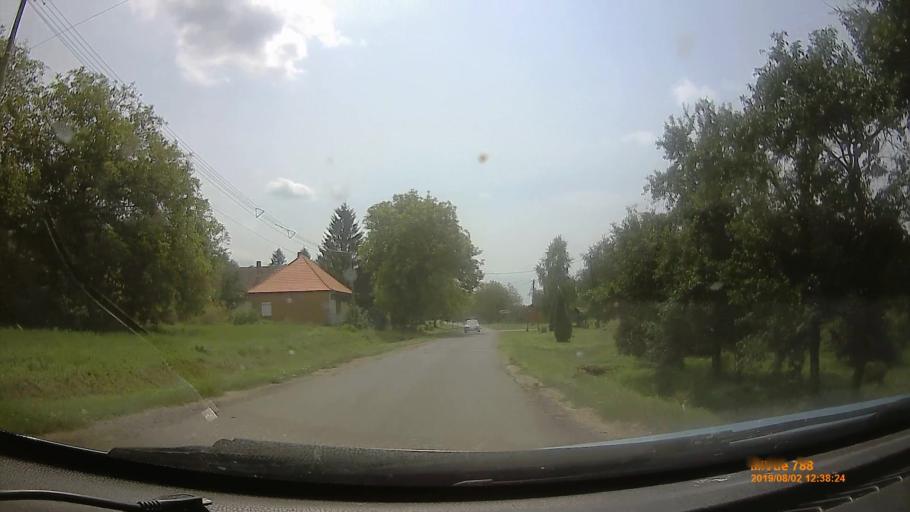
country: HU
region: Baranya
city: Buekkoesd
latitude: 46.0958
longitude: 17.9570
